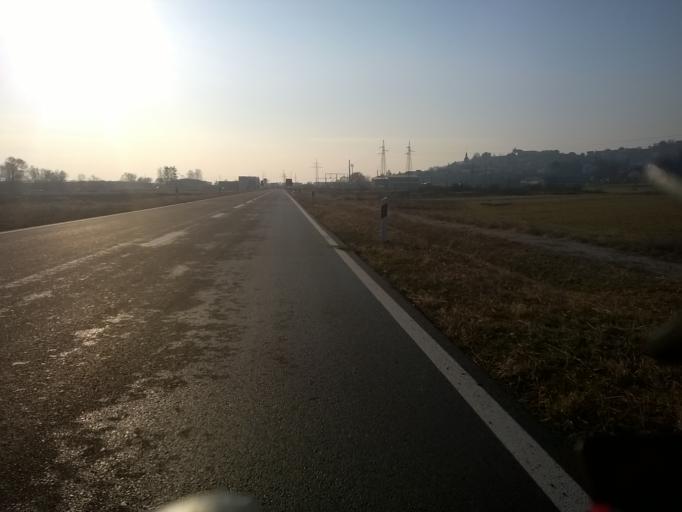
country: HR
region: Krapinsko-Zagorska
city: Zabok
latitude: 46.0316
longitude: 15.9197
